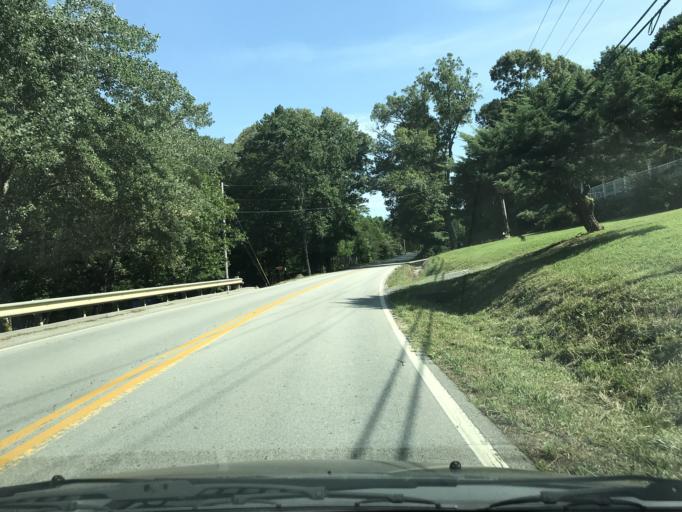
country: US
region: Tennessee
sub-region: Hamilton County
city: Lakesite
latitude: 35.1963
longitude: -85.0707
